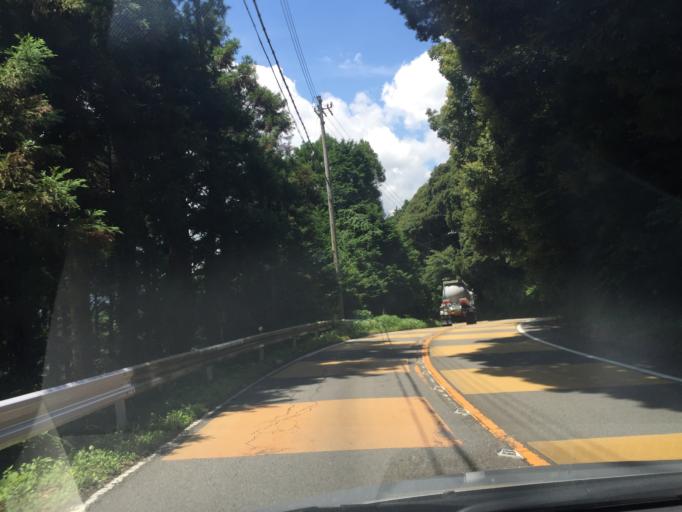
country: JP
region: Shizuoka
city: Kanaya
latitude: 34.8203
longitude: 138.1136
